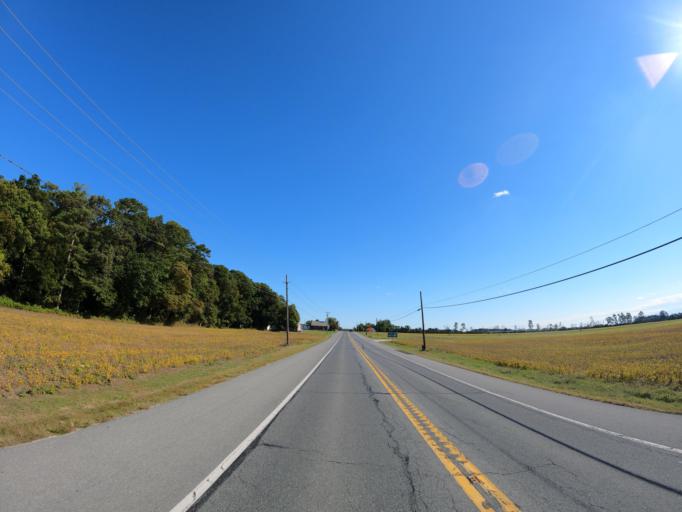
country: US
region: Delaware
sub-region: Sussex County
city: Milton
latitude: 38.8009
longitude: -75.2801
